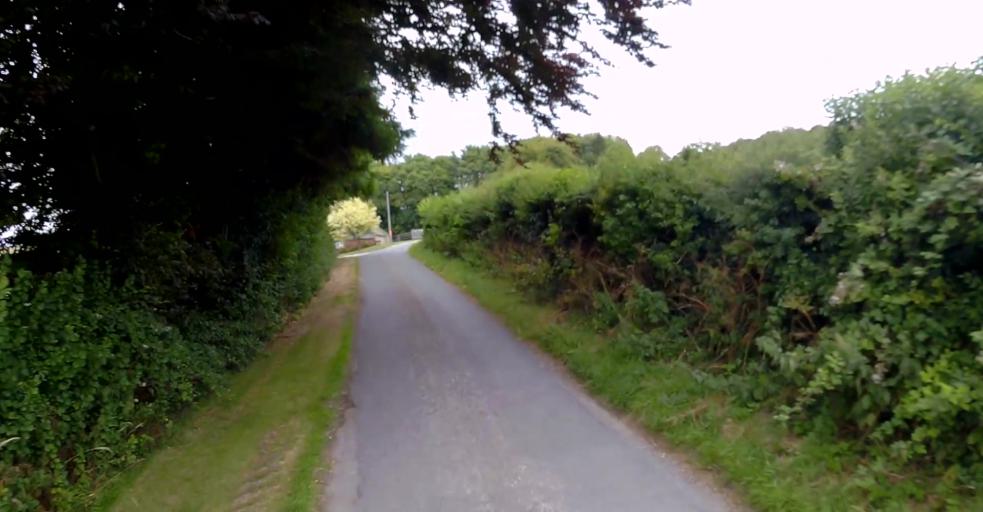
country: GB
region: England
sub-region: Hampshire
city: Kings Worthy
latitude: 51.0550
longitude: -1.2099
